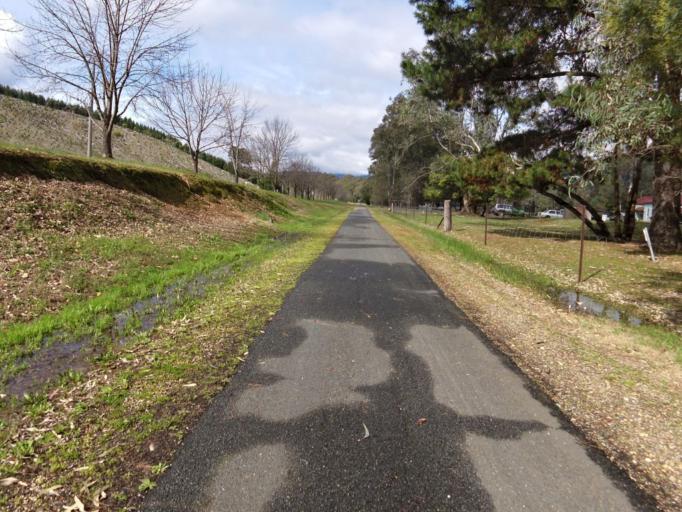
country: AU
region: Victoria
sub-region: Alpine
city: Mount Beauty
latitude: -36.5778
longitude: 146.7491
